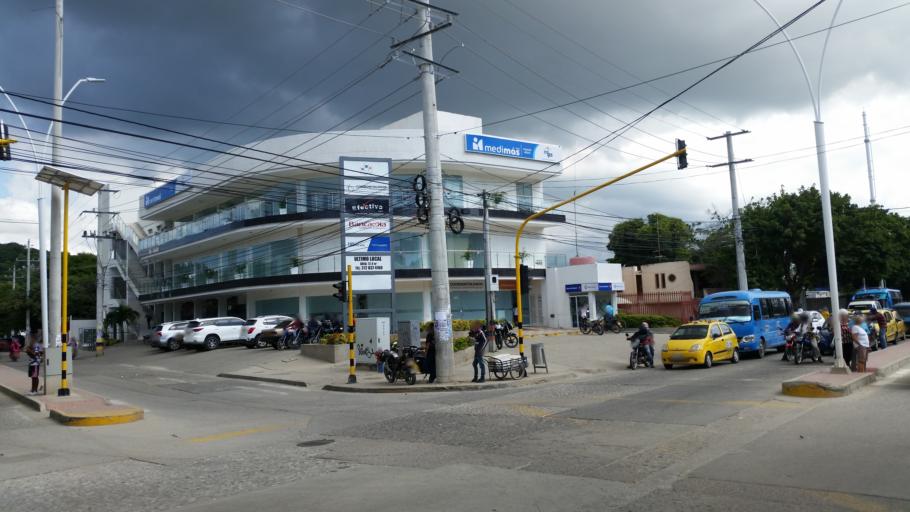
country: CO
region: Magdalena
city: Santa Marta
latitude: 11.2392
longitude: -74.1808
